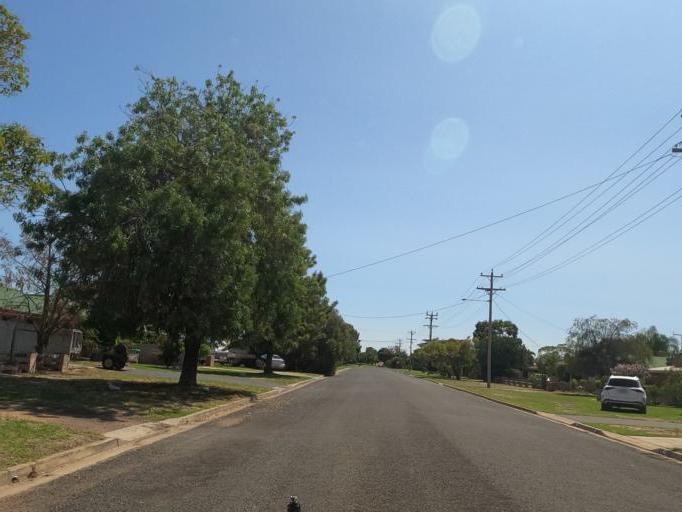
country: AU
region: New South Wales
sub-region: Corowa Shire
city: Mulwala
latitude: -35.9852
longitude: 146.0075
